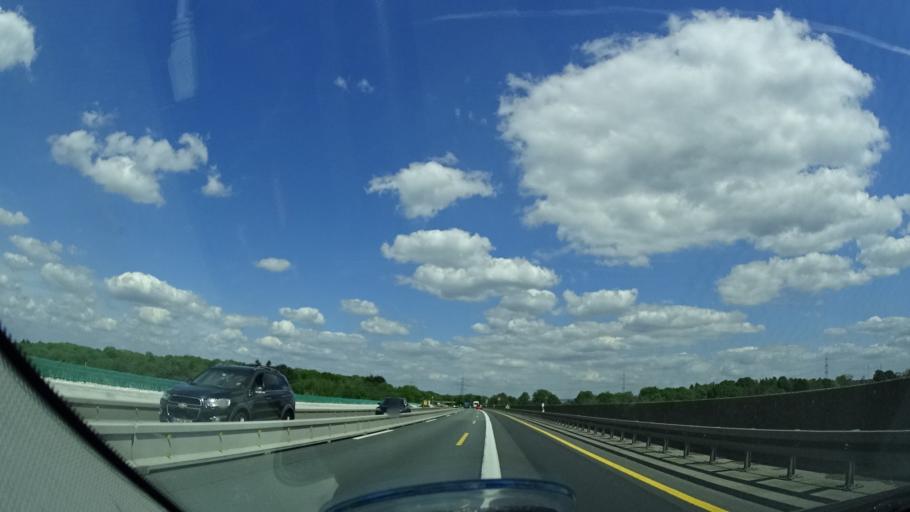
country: DE
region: North Rhine-Westphalia
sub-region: Regierungsbezirk Detmold
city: Paderborn
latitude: 51.6755
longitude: 8.7133
